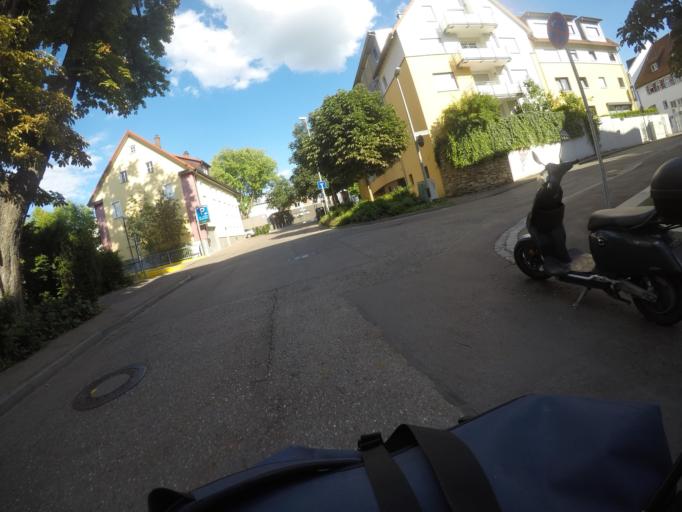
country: DE
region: Baden-Wuerttemberg
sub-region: Regierungsbezirk Stuttgart
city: Nurtingen
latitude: 48.6276
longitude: 9.3382
